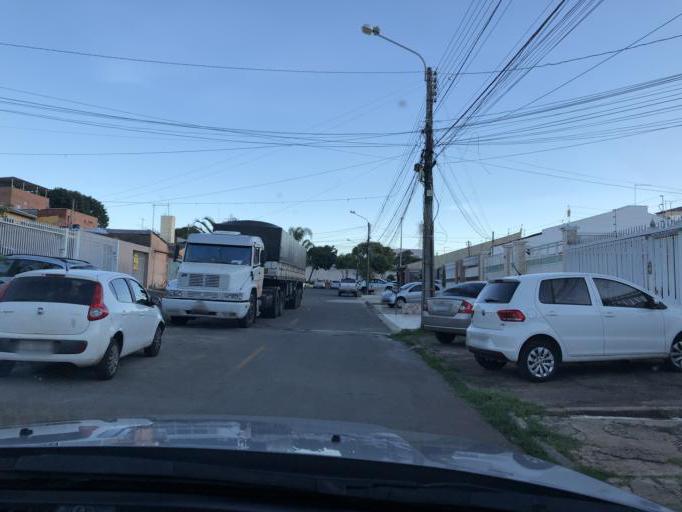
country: BR
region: Federal District
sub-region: Brasilia
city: Brasilia
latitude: -15.8489
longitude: -48.0487
